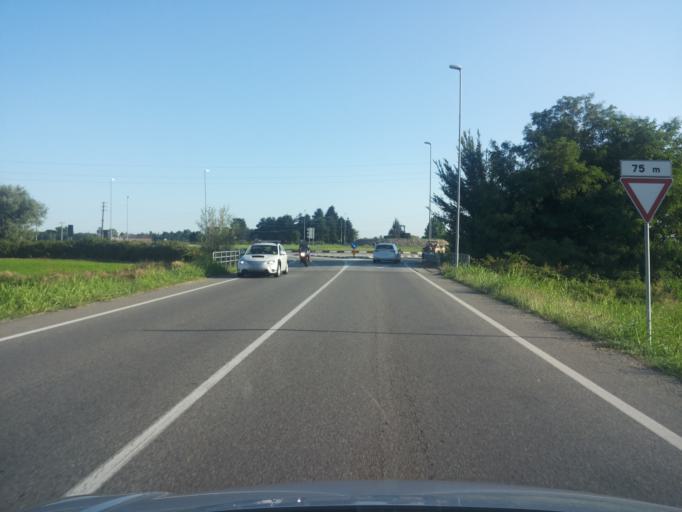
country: IT
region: Piedmont
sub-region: Provincia di Vercelli
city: Caresanablot
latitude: 45.3427
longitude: 8.3945
